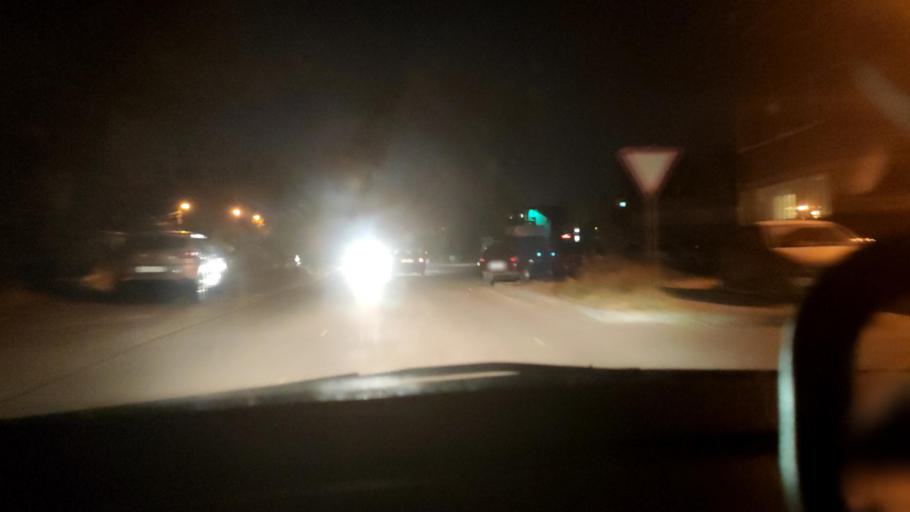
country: RU
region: Voronezj
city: Voronezh
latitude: 51.6711
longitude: 39.1653
